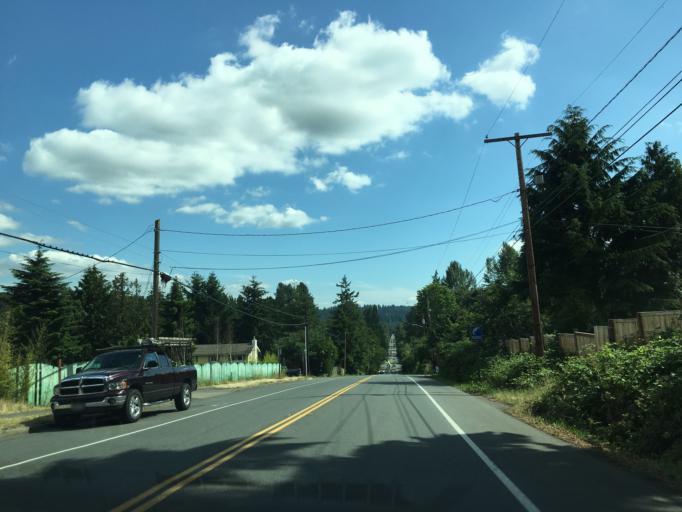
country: US
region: Washington
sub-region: King County
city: Kenmore
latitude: 47.7757
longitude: -122.2331
